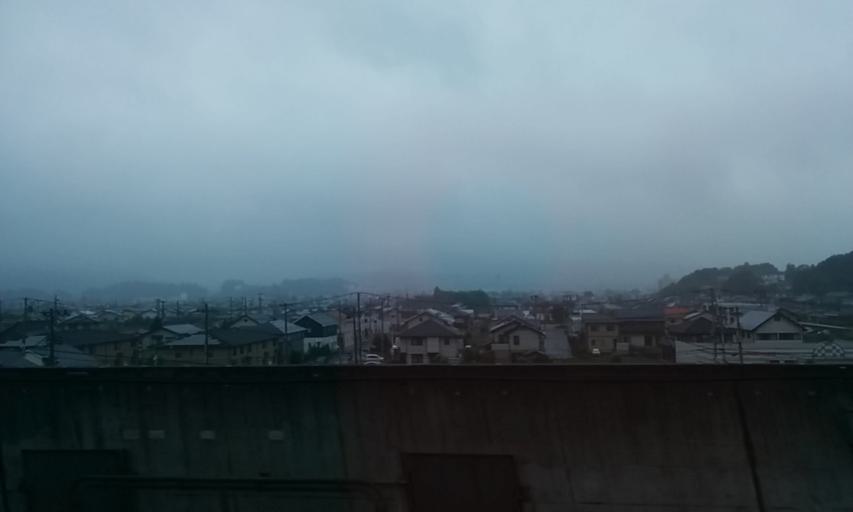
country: JP
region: Miyagi
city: Shiroishi
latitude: 37.9974
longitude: 140.6349
